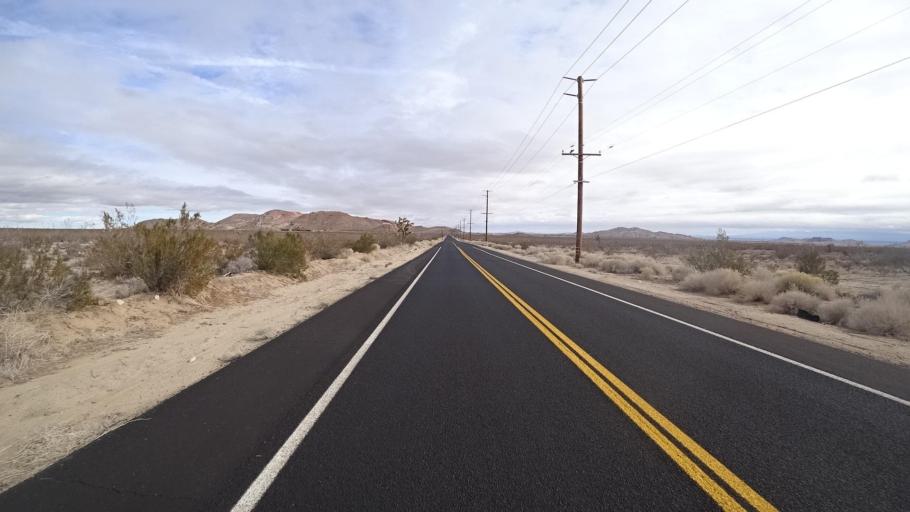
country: US
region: California
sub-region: Kern County
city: Mojave
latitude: 34.9509
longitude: -118.3081
